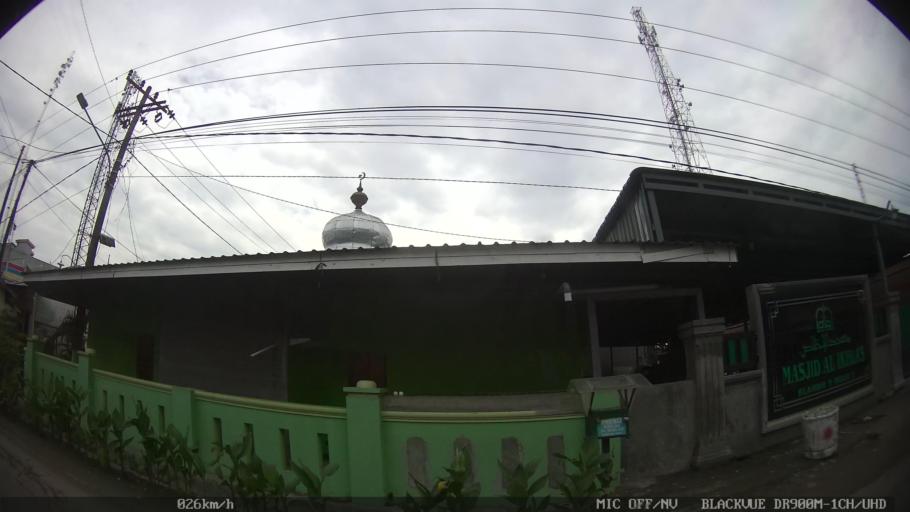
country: ID
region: North Sumatra
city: Sunggal
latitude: 3.6430
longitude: 98.5941
